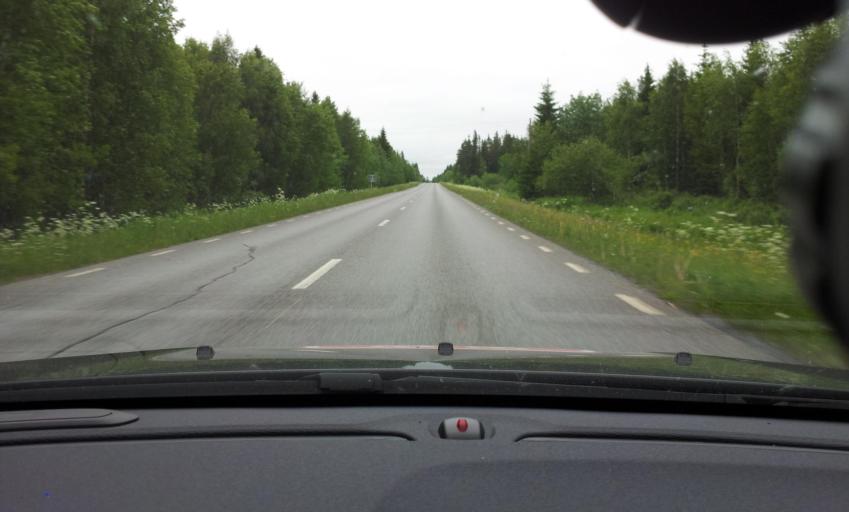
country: SE
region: Jaemtland
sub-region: Krokoms Kommun
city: Valla
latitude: 63.2280
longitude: 14.0152
